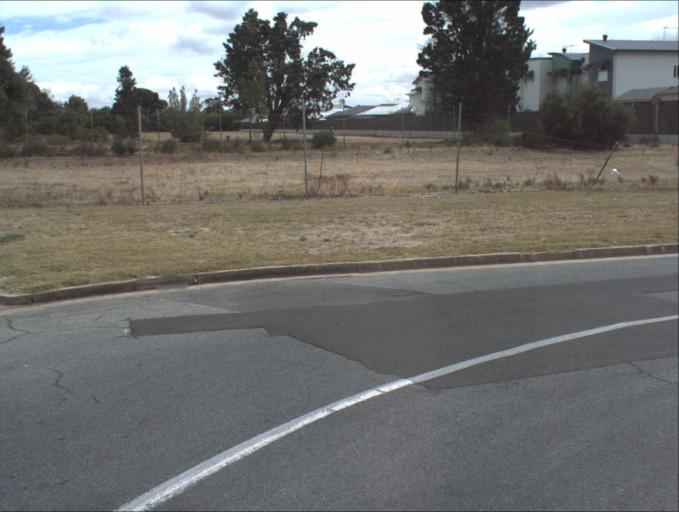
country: AU
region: South Australia
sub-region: Port Adelaide Enfield
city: Birkenhead
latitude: -34.8144
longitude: 138.5036
